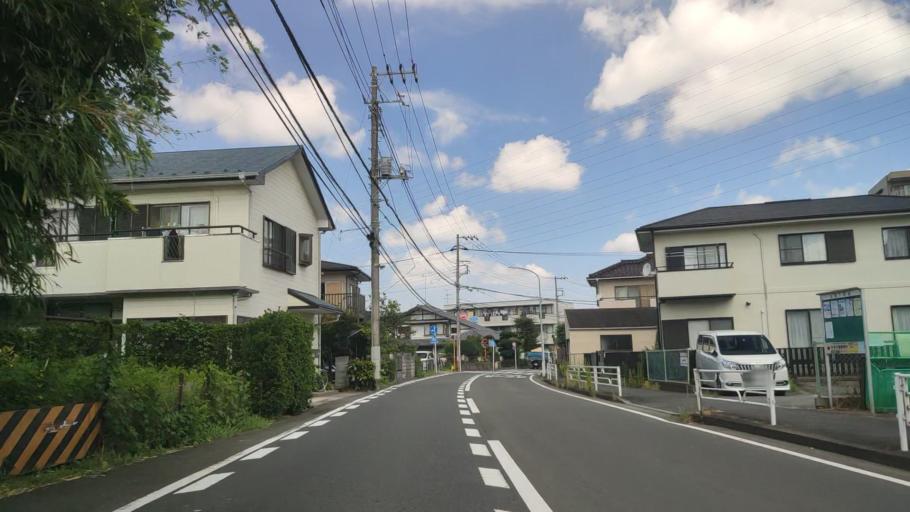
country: JP
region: Kanagawa
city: Yokohama
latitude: 35.5315
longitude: 139.6201
